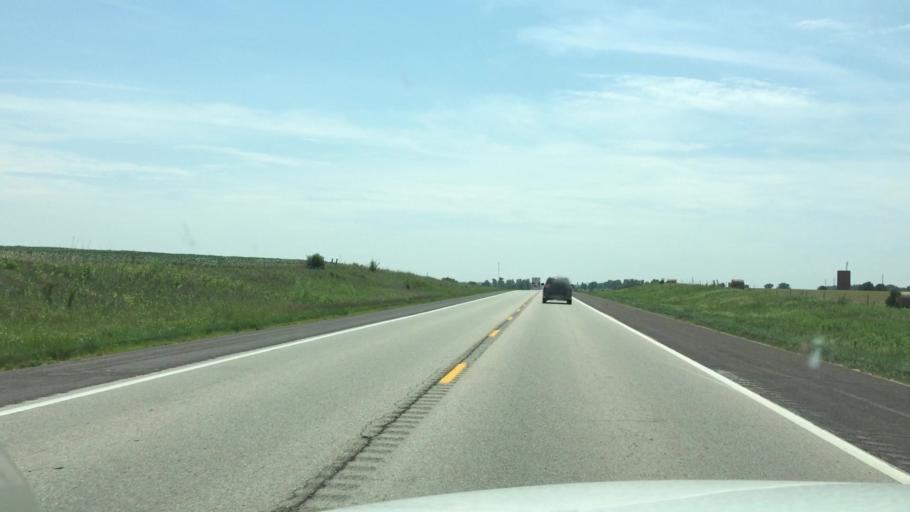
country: US
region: Kansas
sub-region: Jackson County
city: Holton
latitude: 39.5114
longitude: -95.7481
